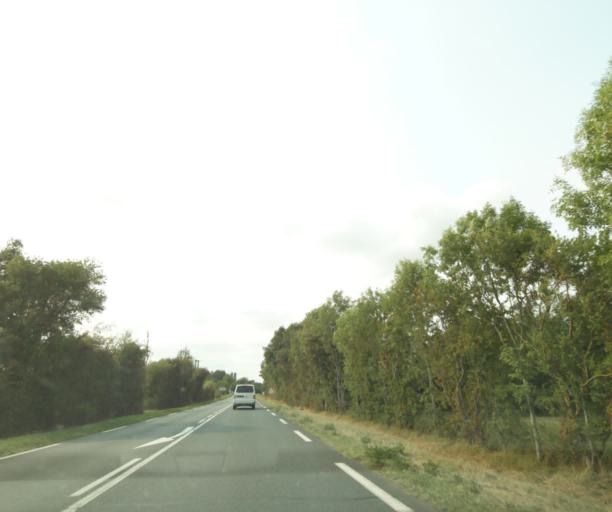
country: FR
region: Centre
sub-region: Departement de l'Indre
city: Chatillon-sur-Indre
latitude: 46.9743
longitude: 1.1856
